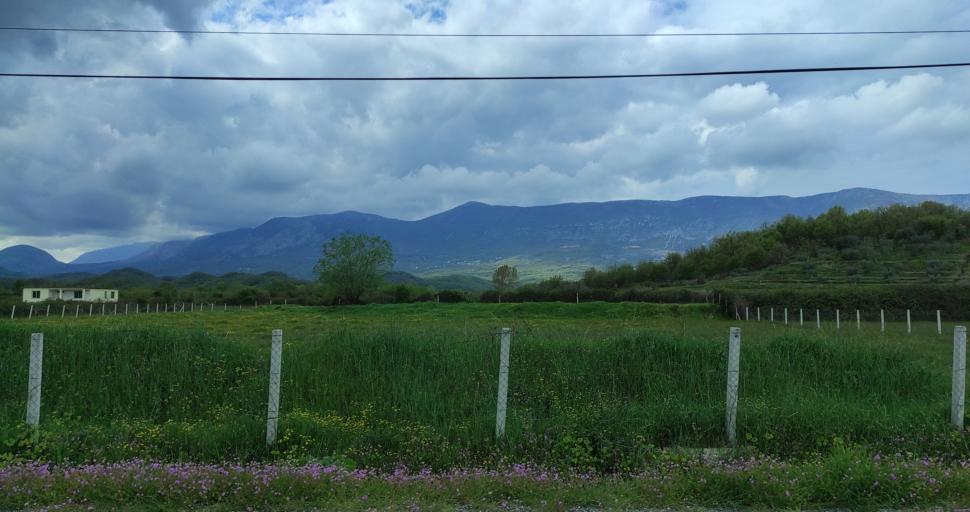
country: AL
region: Shkoder
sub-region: Rrethi i Shkodres
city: Dajc
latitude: 42.0206
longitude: 19.3781
